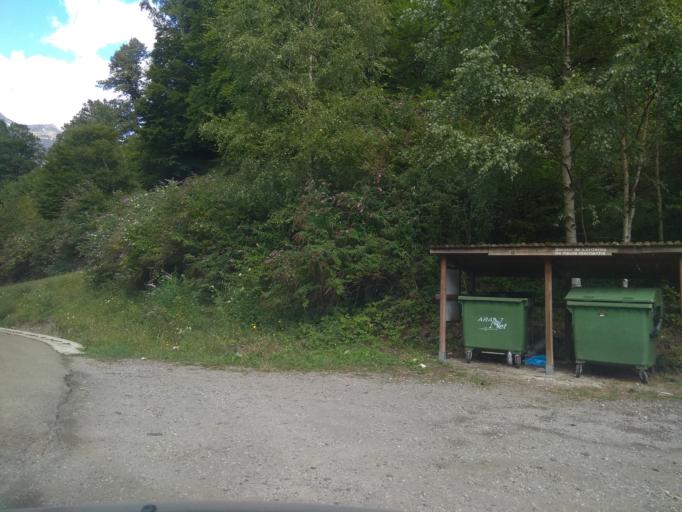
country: ES
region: Catalonia
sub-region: Provincia de Lleida
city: Vielha
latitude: 42.7191
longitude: 0.7242
